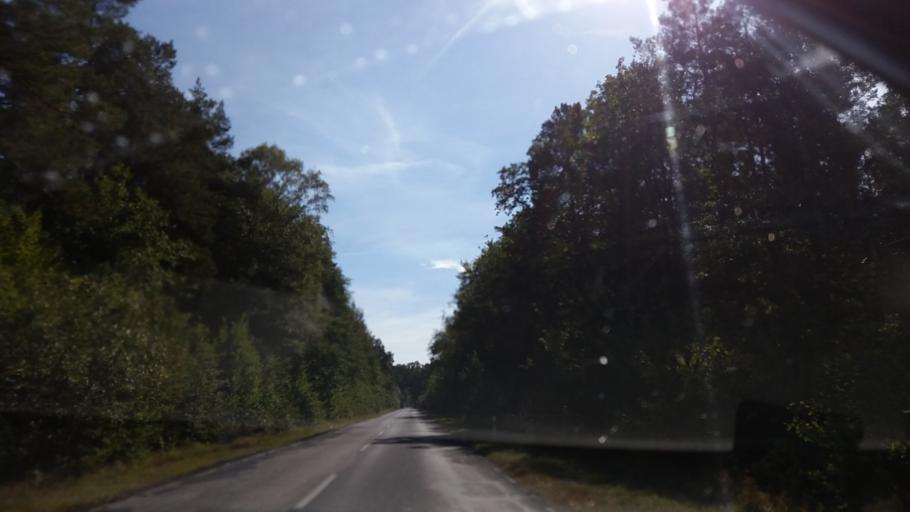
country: PL
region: Lubusz
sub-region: Powiat strzelecko-drezdenecki
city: Drezdenko
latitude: 52.7971
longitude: 15.8339
